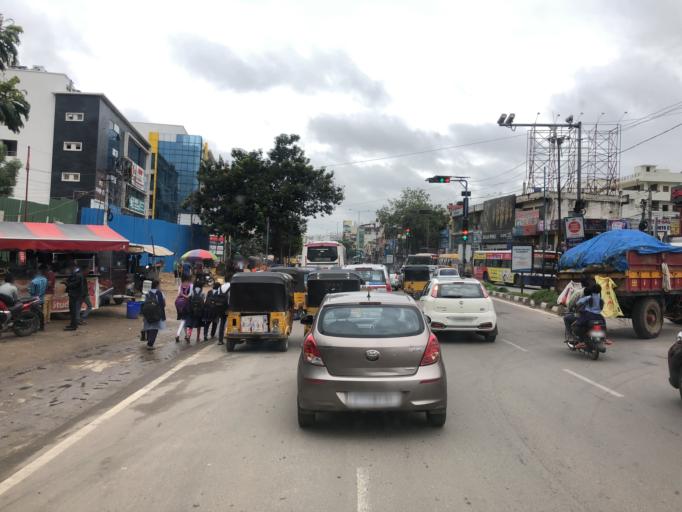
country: IN
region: Telangana
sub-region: Rangareddi
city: Kukatpalli
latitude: 17.4644
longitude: 78.3674
